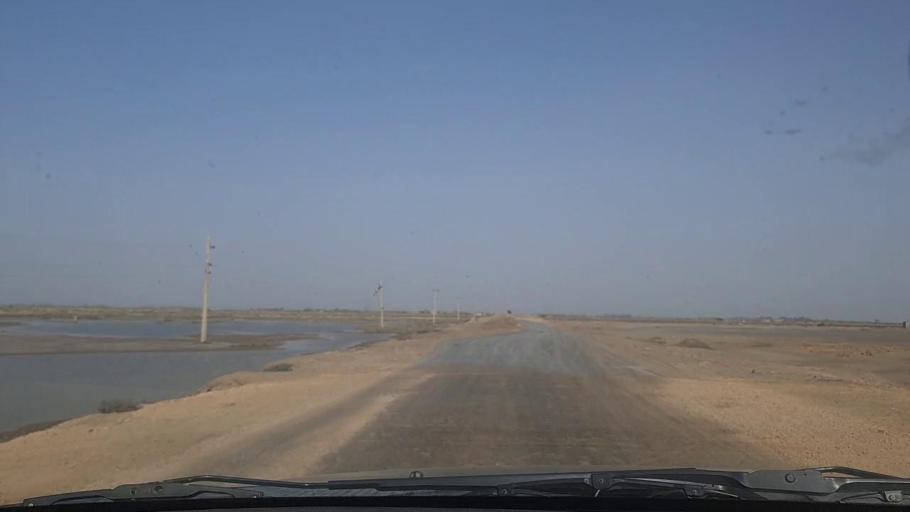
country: PK
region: Sindh
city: Keti Bandar
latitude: 24.1560
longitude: 67.5157
